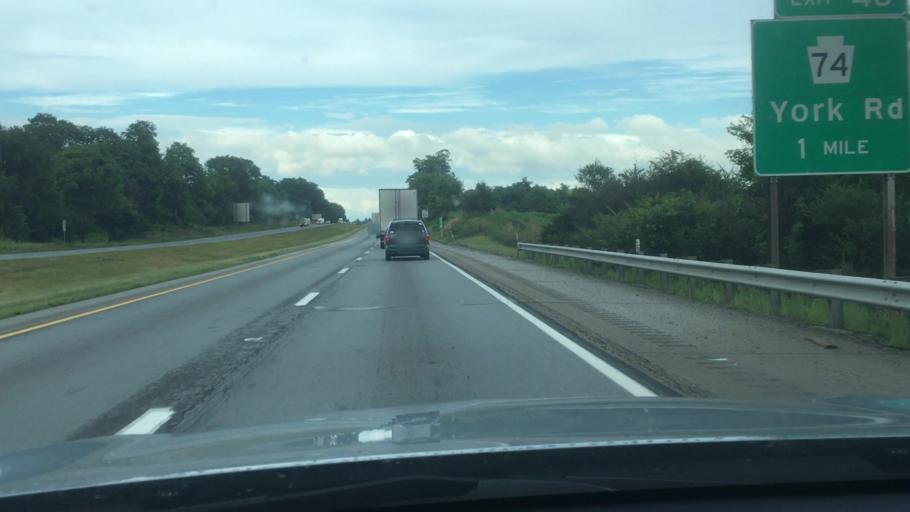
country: US
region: Pennsylvania
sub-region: Cumberland County
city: Carlisle
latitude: 40.1885
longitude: -77.1837
